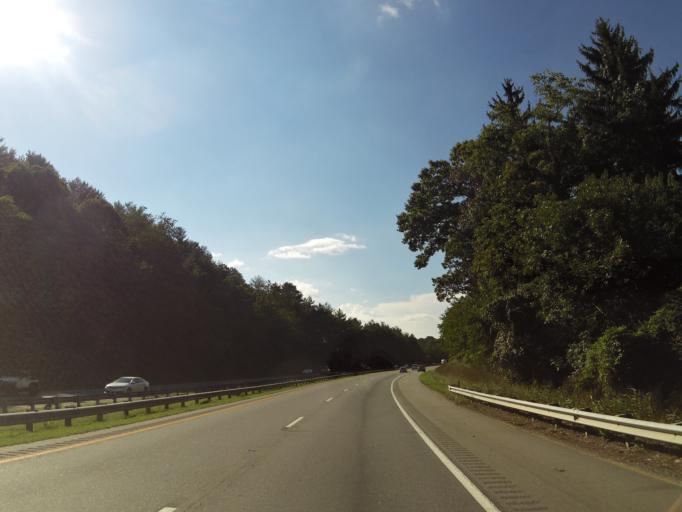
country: US
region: North Carolina
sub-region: Buncombe County
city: Asheville
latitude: 35.5582
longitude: -82.5672
